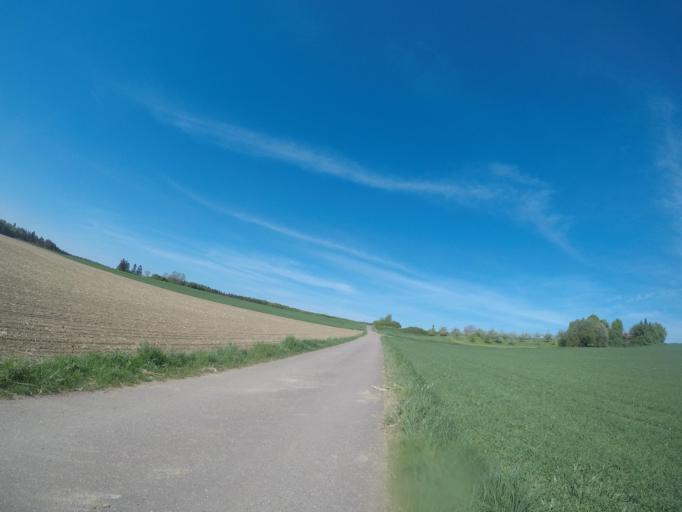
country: DE
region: Baden-Wuerttemberg
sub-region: Tuebingen Region
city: Berghulen
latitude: 48.4828
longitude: 9.7421
